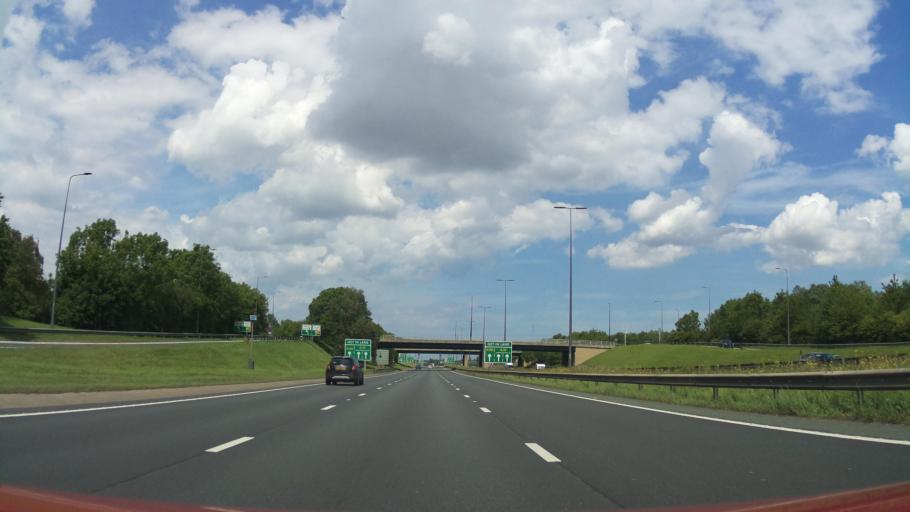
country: GB
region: England
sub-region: Redcar and Cleveland
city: Thornaby-on-Tees
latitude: 54.5464
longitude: -1.2763
